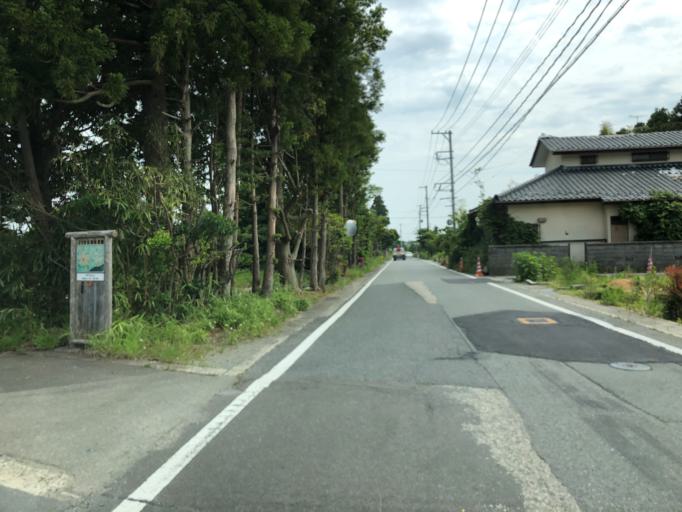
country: JP
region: Fukushima
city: Namie
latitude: 37.2986
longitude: 140.9992
